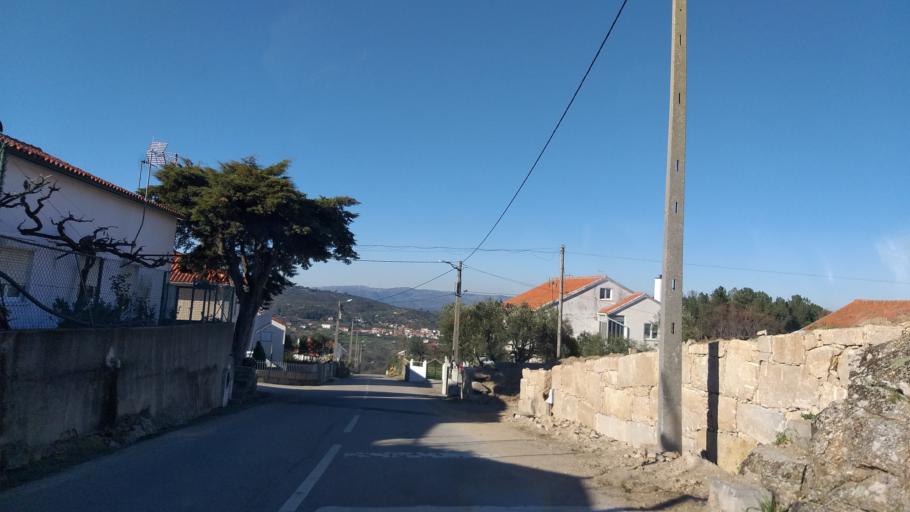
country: PT
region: Guarda
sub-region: Celorico da Beira
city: Celorico da Beira
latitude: 40.5852
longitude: -7.3601
